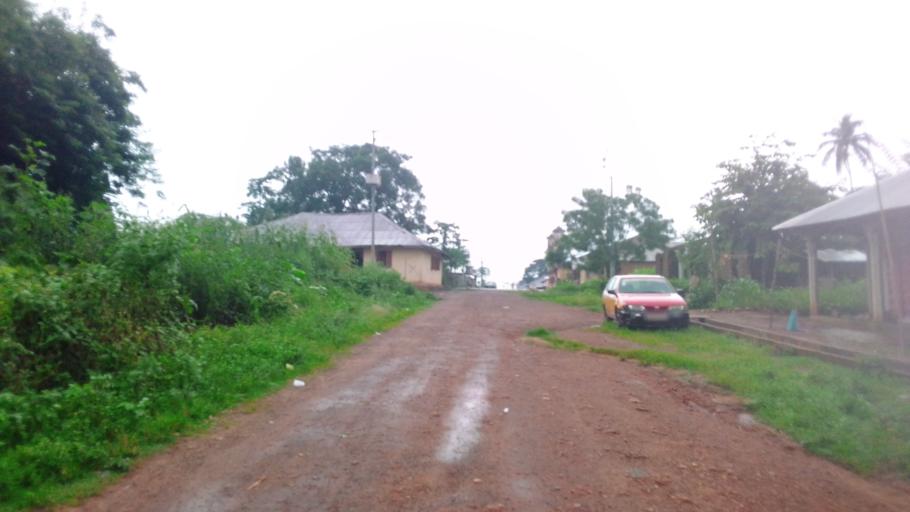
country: SL
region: Northern Province
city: Lunsar
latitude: 8.6830
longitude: -12.5304
